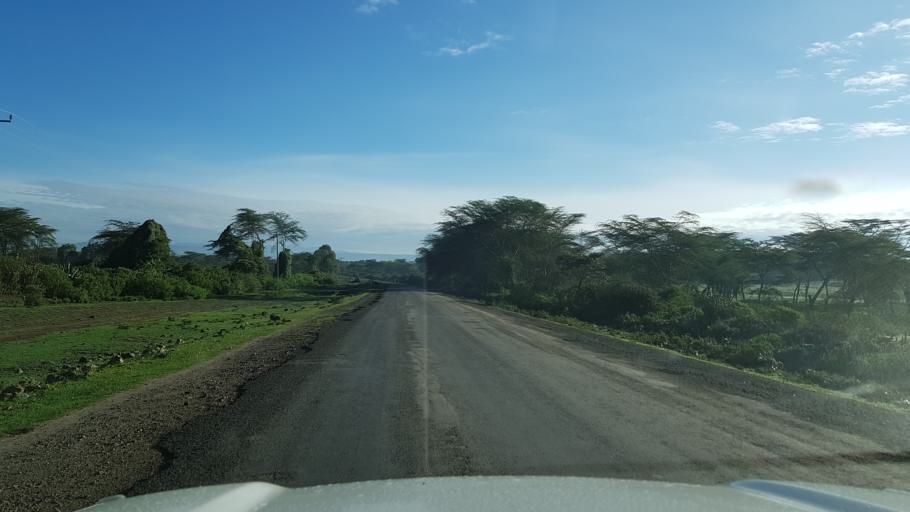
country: KE
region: Nakuru
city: Naivasha
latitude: -0.7976
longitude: 36.4212
